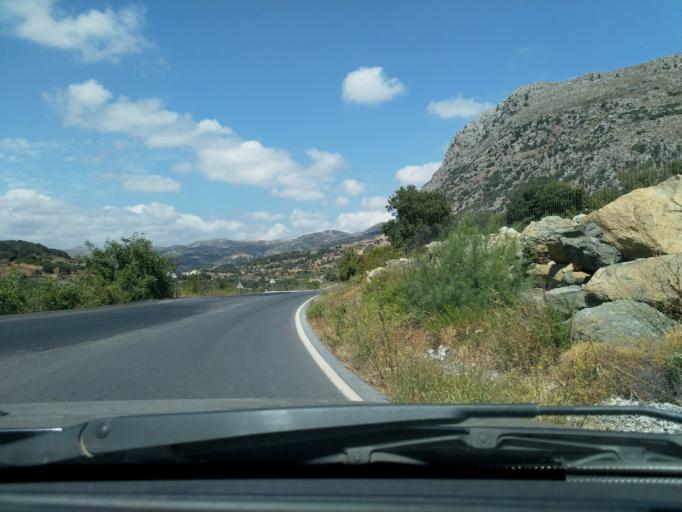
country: GR
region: Crete
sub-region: Nomos Rethymnis
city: Agia Foteini
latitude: 35.1986
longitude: 24.5441
